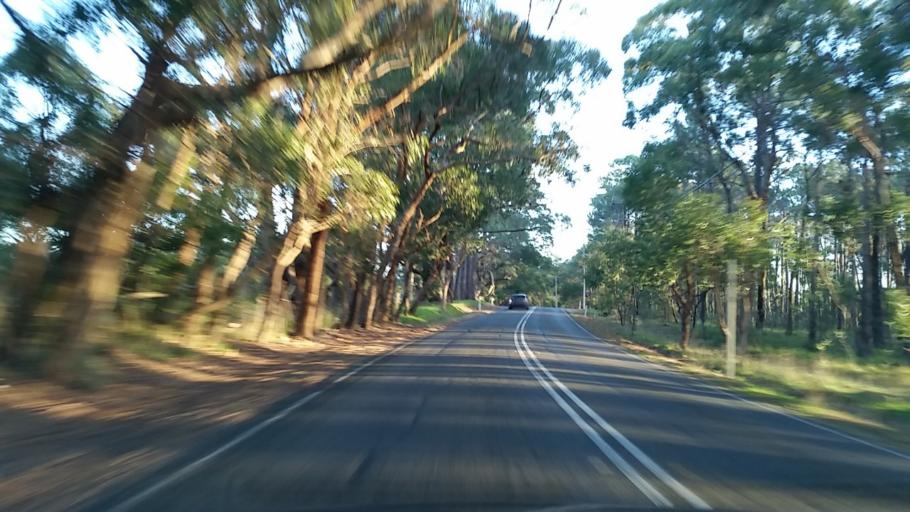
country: AU
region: South Australia
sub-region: Adelaide Hills
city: Upper Sturt
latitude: -35.0619
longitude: 138.6770
